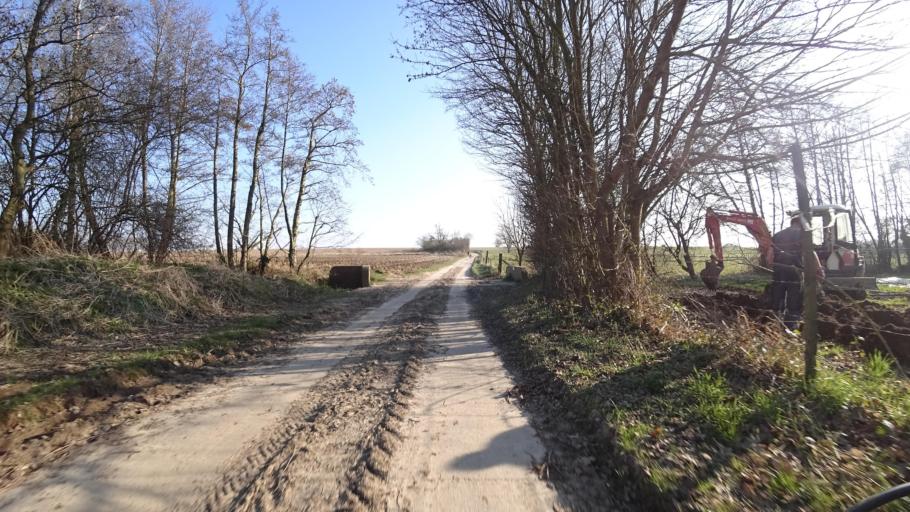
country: BE
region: Wallonia
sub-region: Province du Brabant Wallon
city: Chastre-Villeroux-Blanmont
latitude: 50.6242
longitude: 4.6526
